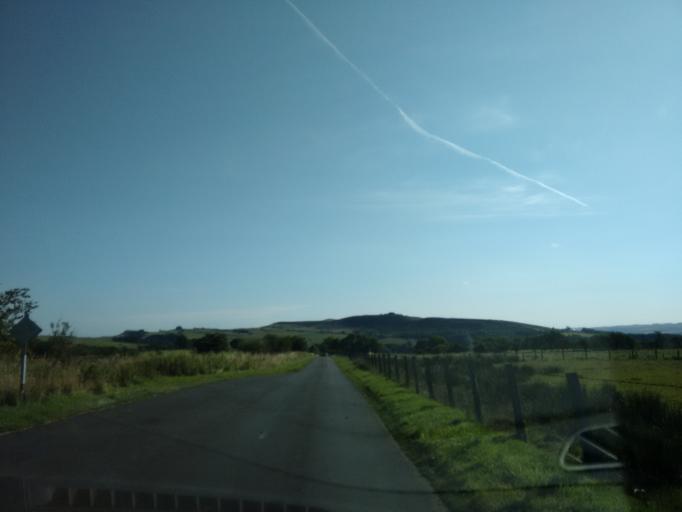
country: GB
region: England
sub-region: Northumberland
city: Bardon Mill
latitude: 54.9905
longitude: -2.3774
